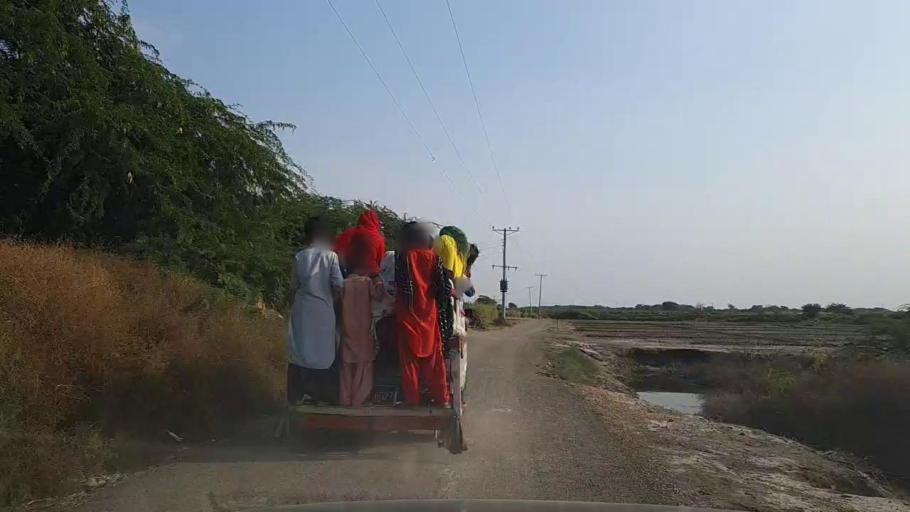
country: PK
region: Sindh
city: Thatta
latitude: 24.6430
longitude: 67.9489
